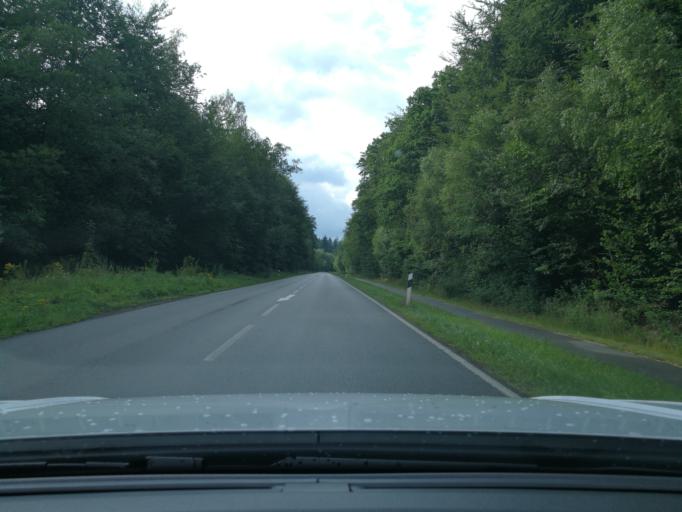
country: DE
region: Schleswig-Holstein
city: Dassendorf
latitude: 53.5112
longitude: 10.3622
